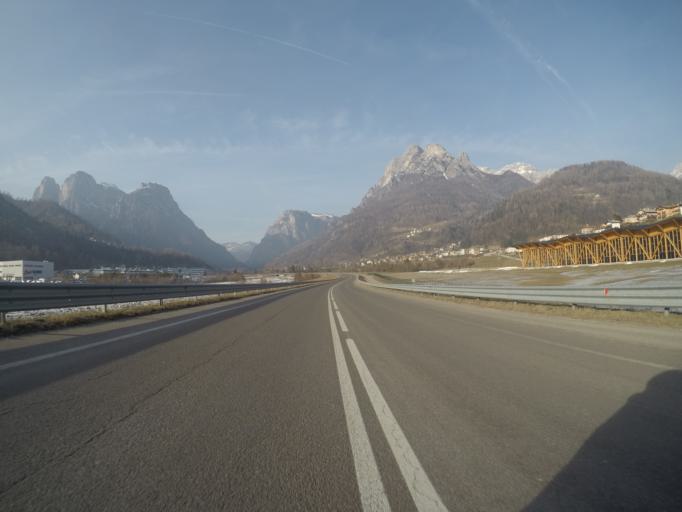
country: IT
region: Veneto
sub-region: Provincia di Belluno
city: Agordo
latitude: 46.2792
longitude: 12.0294
